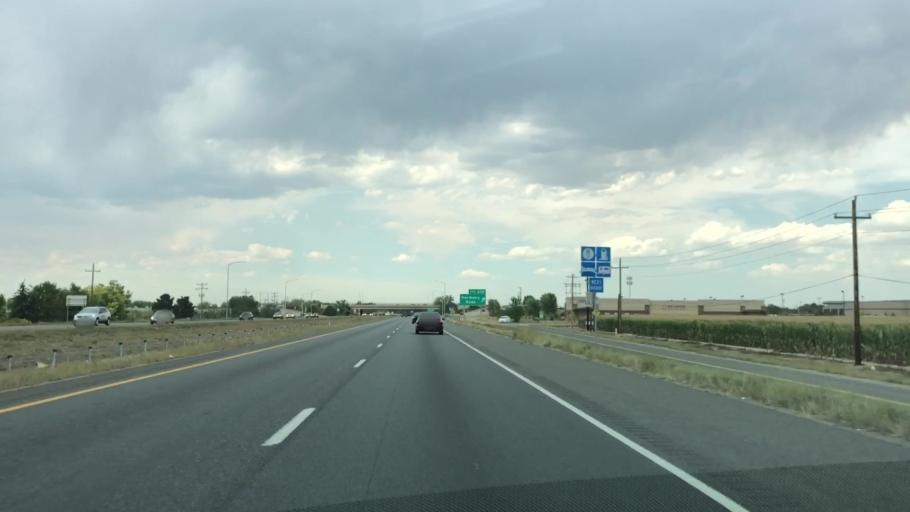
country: US
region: Colorado
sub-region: Weld County
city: Windsor
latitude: 40.5171
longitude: -104.9913
